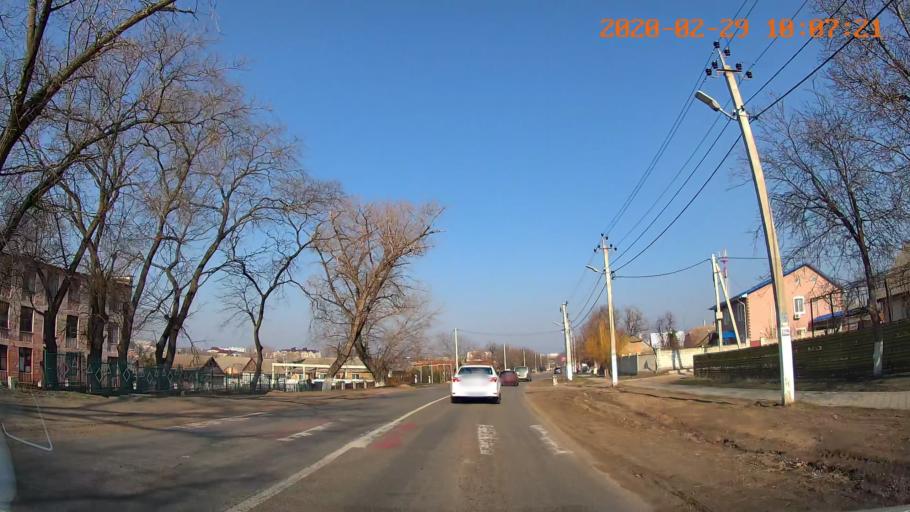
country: MD
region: Telenesti
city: Tiraspolul Nou
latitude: 46.8205
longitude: 29.6655
